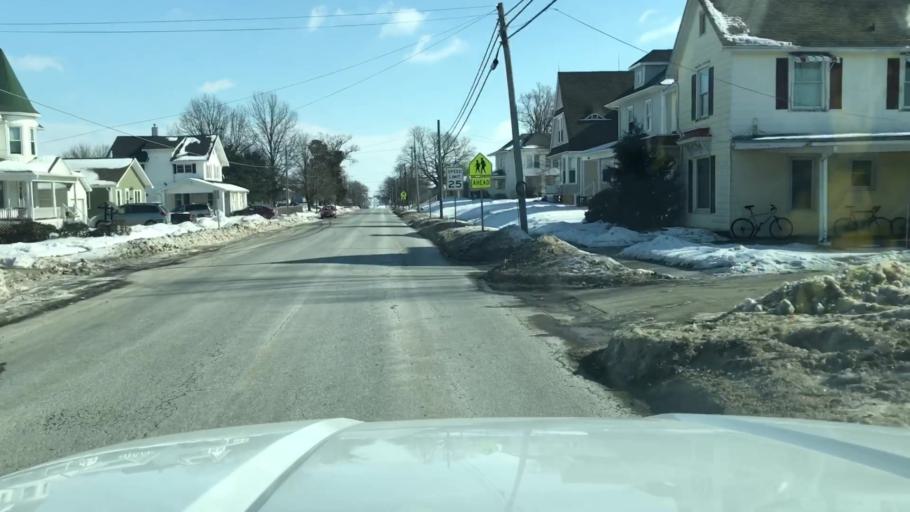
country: US
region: Missouri
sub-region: Nodaway County
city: Maryville
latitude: 40.3455
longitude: -94.8692
